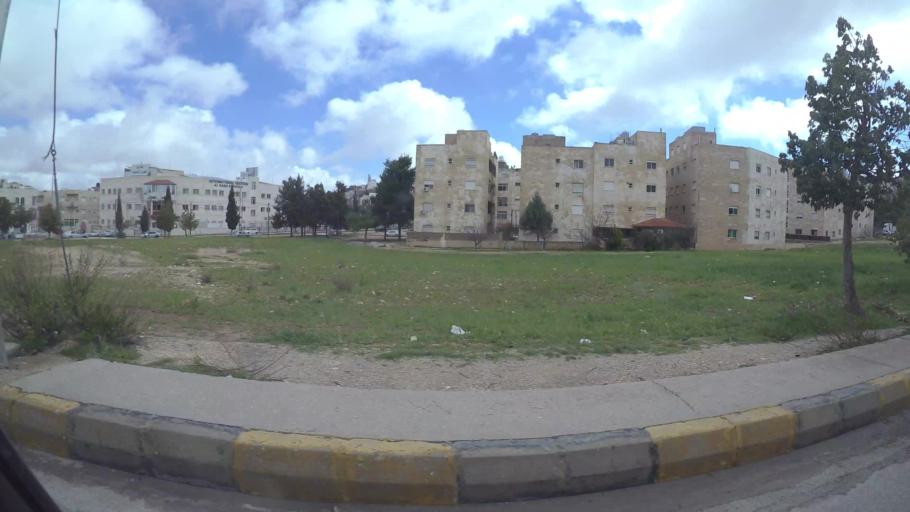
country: JO
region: Amman
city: Al Jubayhah
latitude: 32.0564
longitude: 35.8708
